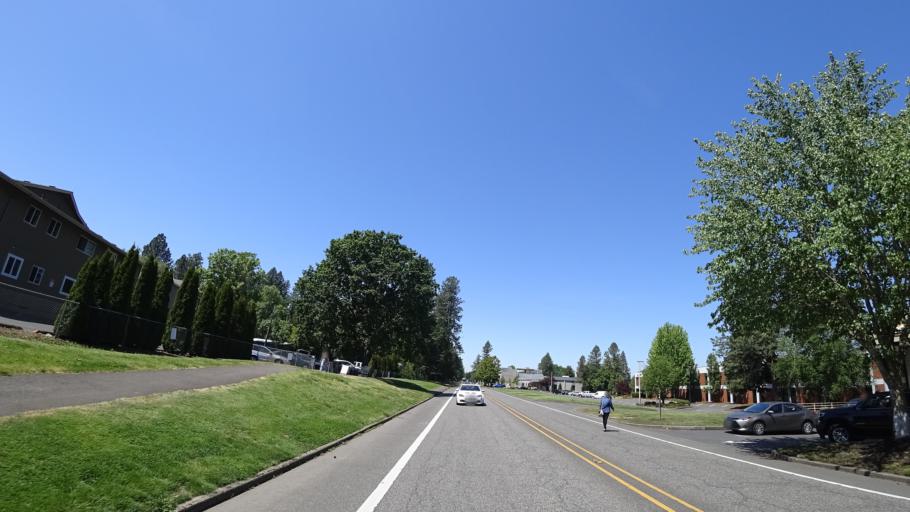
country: US
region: Oregon
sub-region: Washington County
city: Beaverton
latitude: 45.4924
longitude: -122.8184
